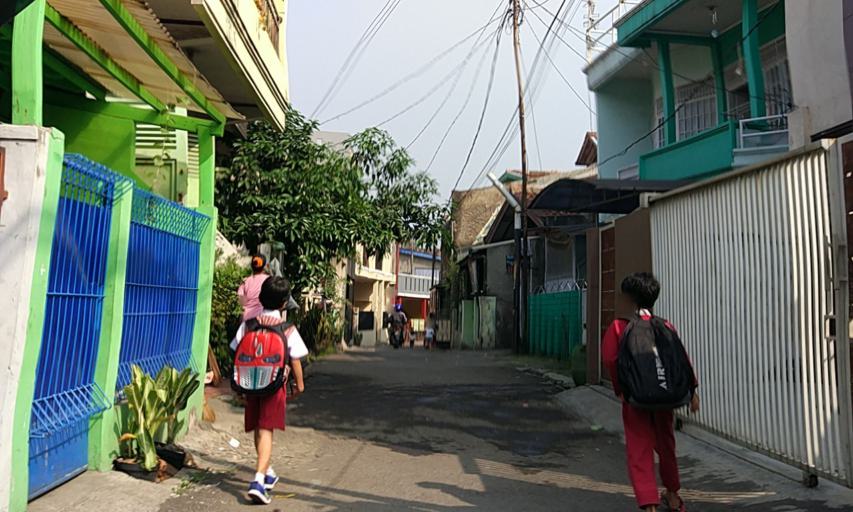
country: ID
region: West Java
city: Bandung
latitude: -6.9028
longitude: 107.6471
